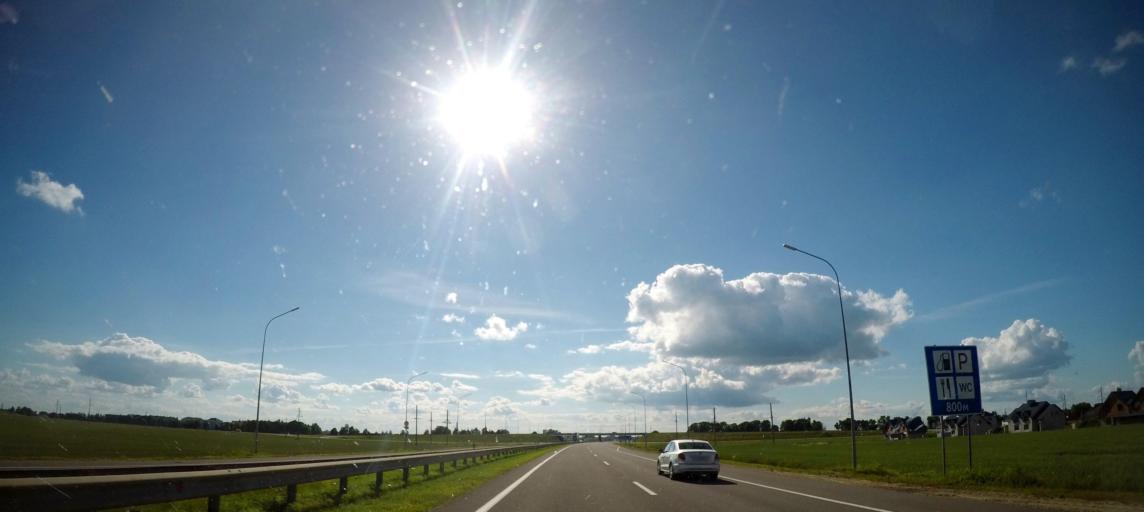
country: BY
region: Grodnenskaya
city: Skidal'
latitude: 53.5772
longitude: 24.2518
